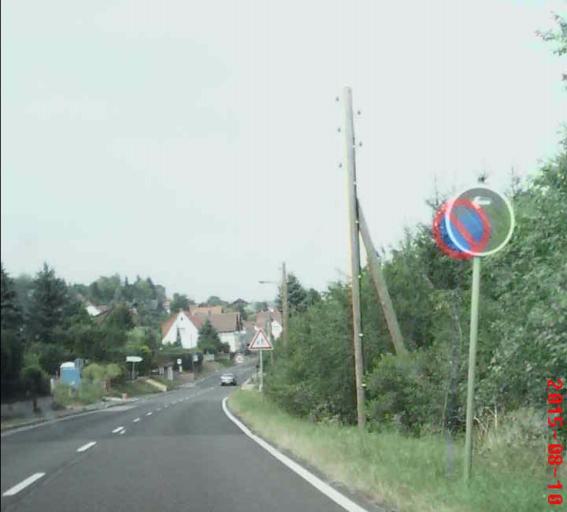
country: DE
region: Thuringia
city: Dillstadt
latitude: 50.5777
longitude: 10.5276
